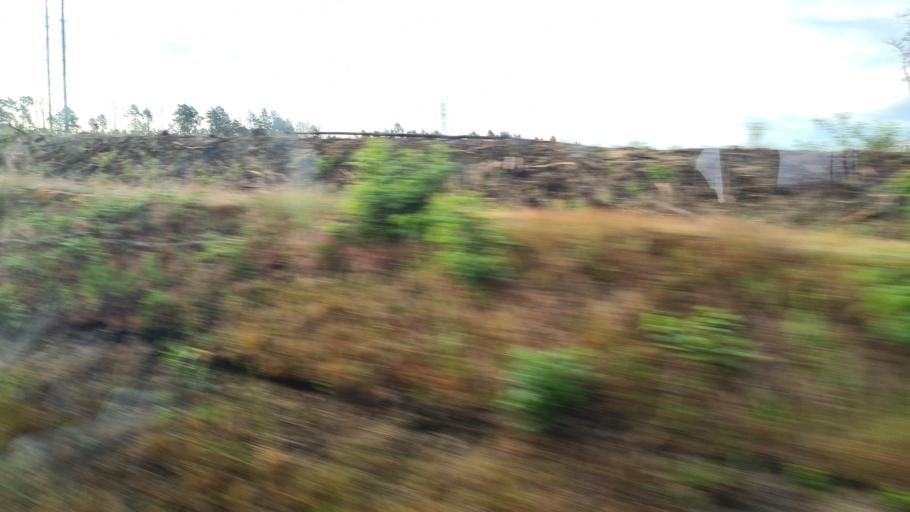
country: DE
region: Brandenburg
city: Finsterwalde
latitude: 51.6295
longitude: 13.6692
